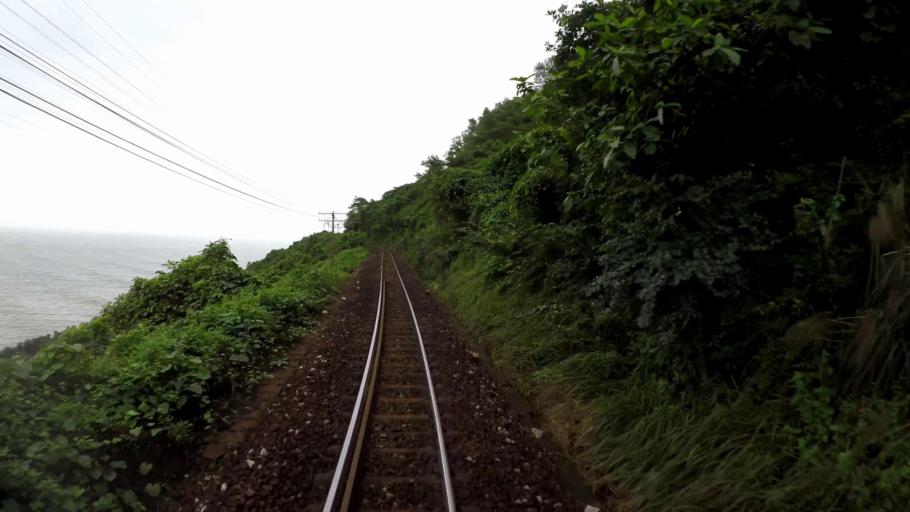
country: VN
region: Da Nang
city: Lien Chieu
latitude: 16.2111
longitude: 108.1230
